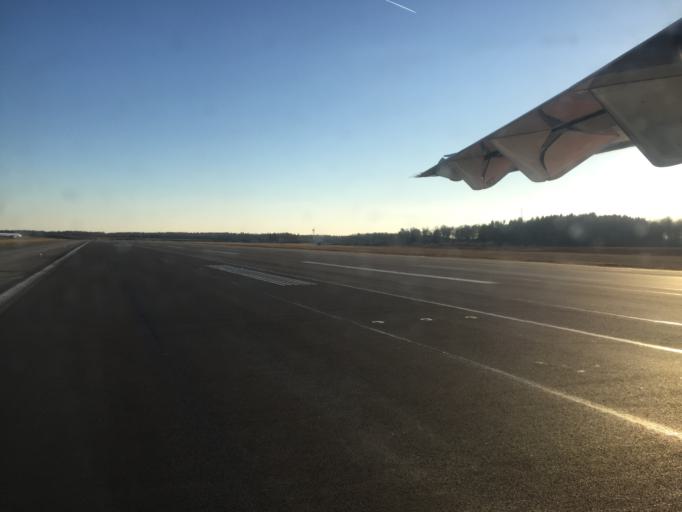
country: SE
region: Stockholm
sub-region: Sigtuna Kommun
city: Marsta
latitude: 59.6443
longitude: 17.9161
